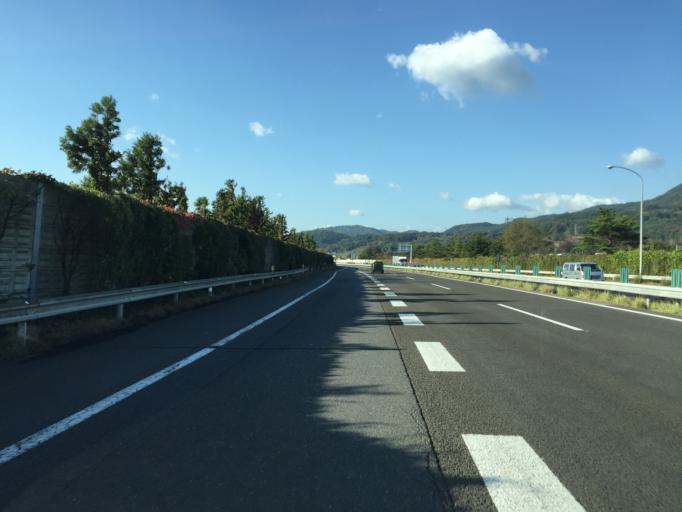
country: JP
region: Fukushima
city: Hobaramachi
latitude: 37.8789
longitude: 140.5286
